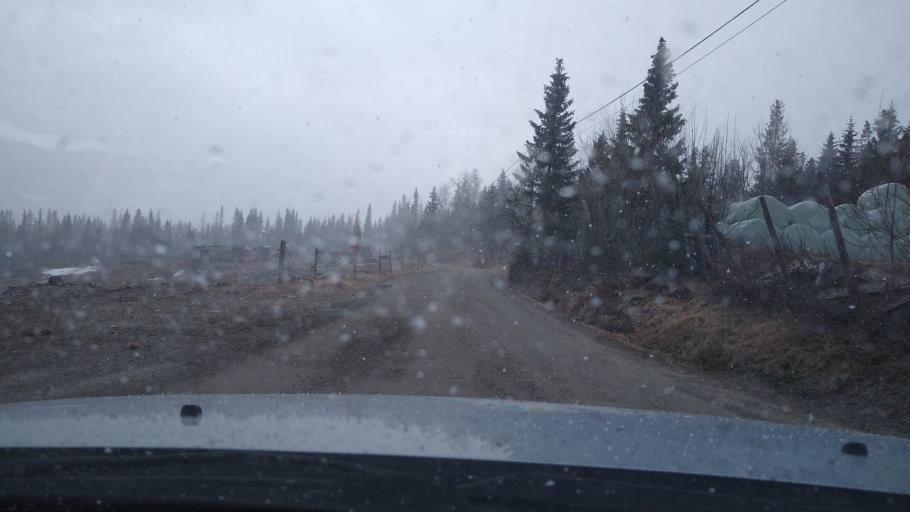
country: NO
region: Oppland
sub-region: Oyer
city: Tretten
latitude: 61.4639
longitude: 10.3456
